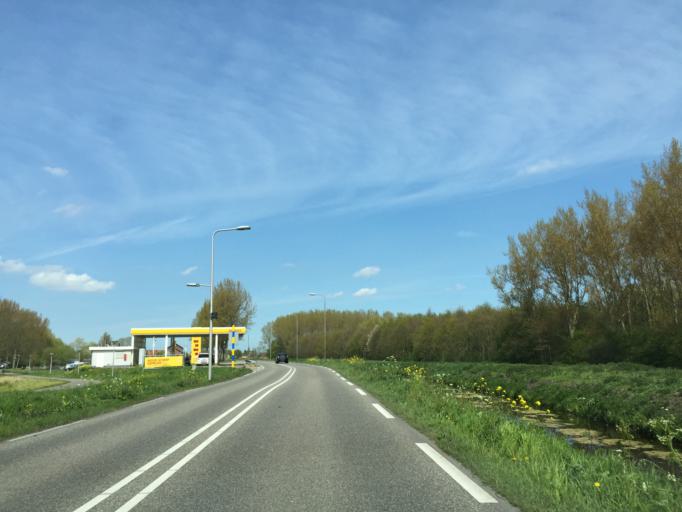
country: NL
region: South Holland
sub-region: Gemeente Pijnacker-Nootdorp
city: Pijnacker
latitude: 52.0300
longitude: 4.4197
